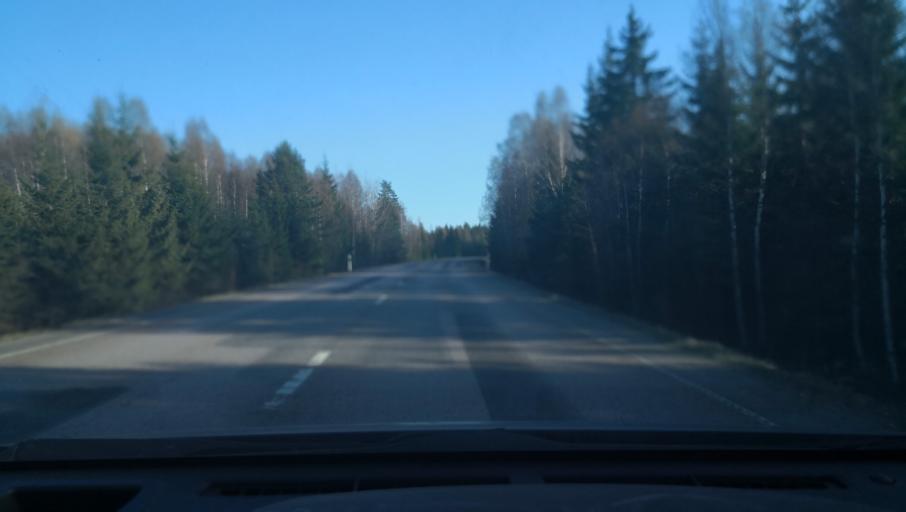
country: SE
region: Uppsala
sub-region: Heby Kommun
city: Heby
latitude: 59.9786
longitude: 16.8361
